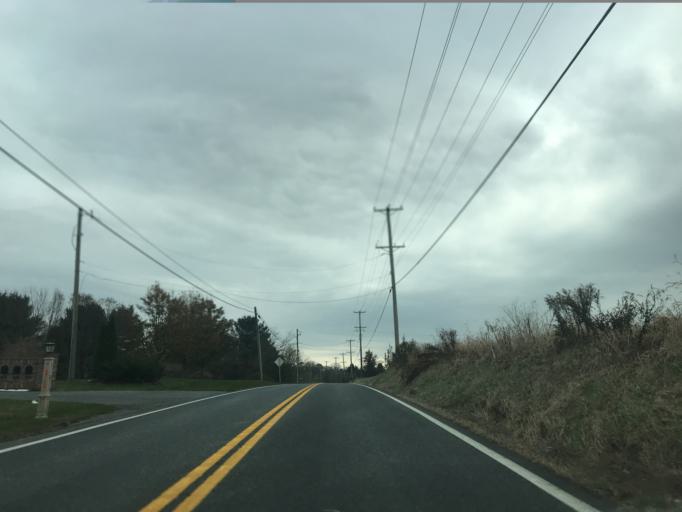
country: US
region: Maryland
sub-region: Harford County
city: Bel Air North
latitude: 39.6486
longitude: -76.3347
